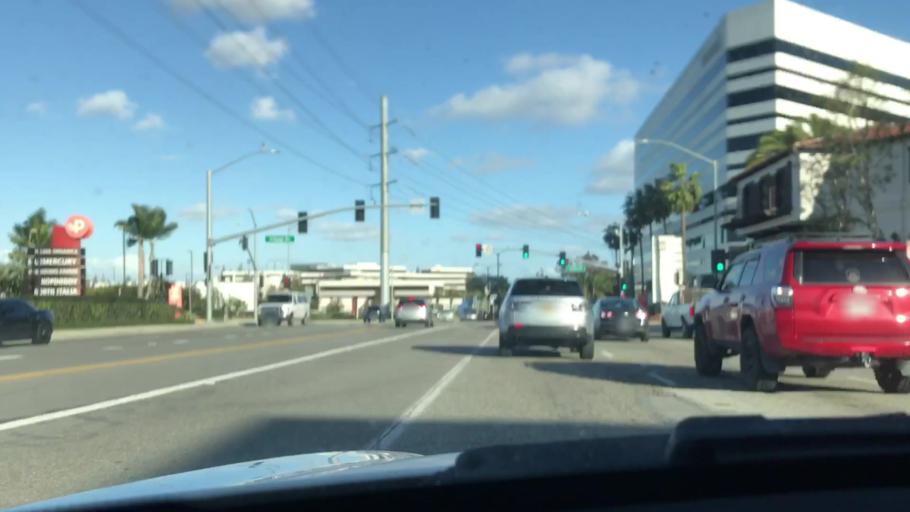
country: US
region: California
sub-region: Los Angeles County
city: Manhattan Beach
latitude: 33.9019
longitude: -118.3936
